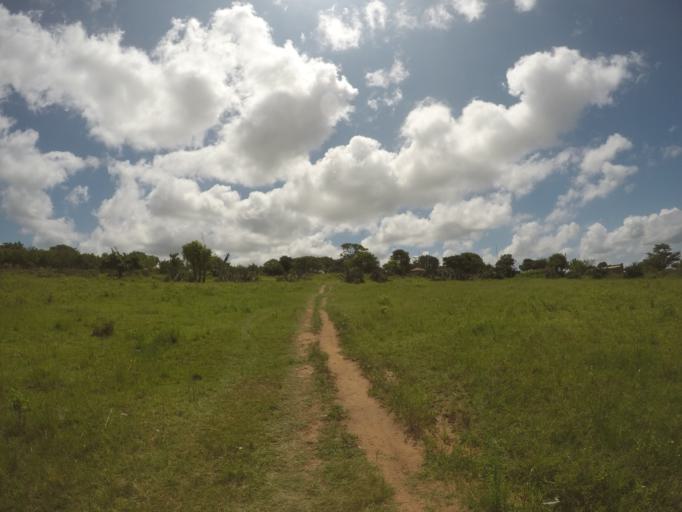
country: ZA
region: KwaZulu-Natal
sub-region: uThungulu District Municipality
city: Empangeni
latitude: -28.5797
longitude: 31.8433
